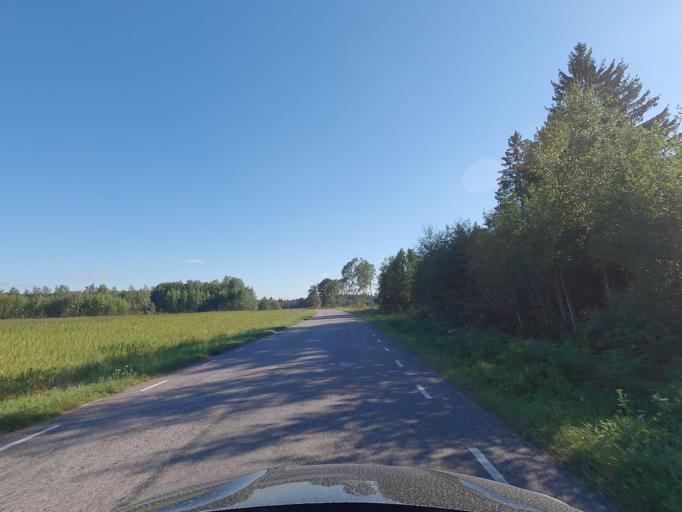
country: EE
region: Raplamaa
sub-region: Kohila vald
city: Kohila
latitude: 59.1444
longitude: 24.6534
